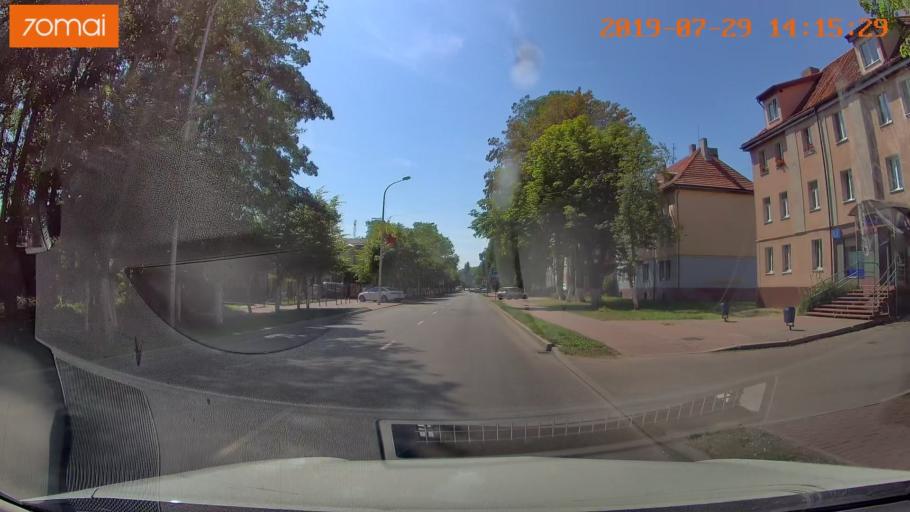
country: RU
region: Kaliningrad
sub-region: Gorod Kaliningrad
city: Baltiysk
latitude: 54.6470
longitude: 19.8998
